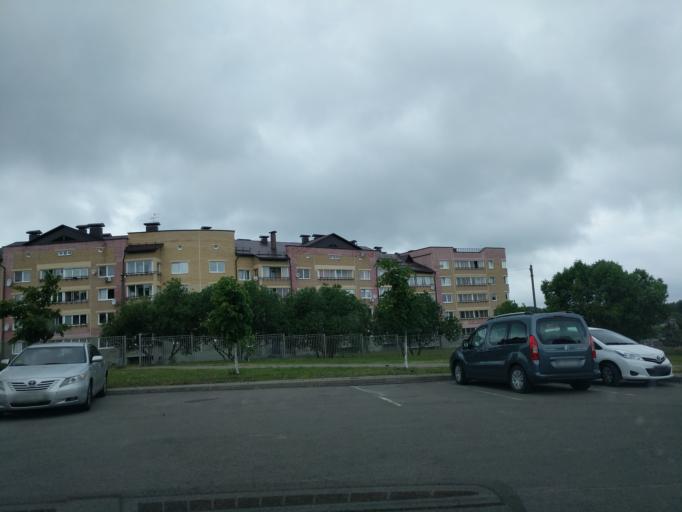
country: BY
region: Minsk
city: Khatsyezhyna
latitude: 53.9372
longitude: 27.3549
